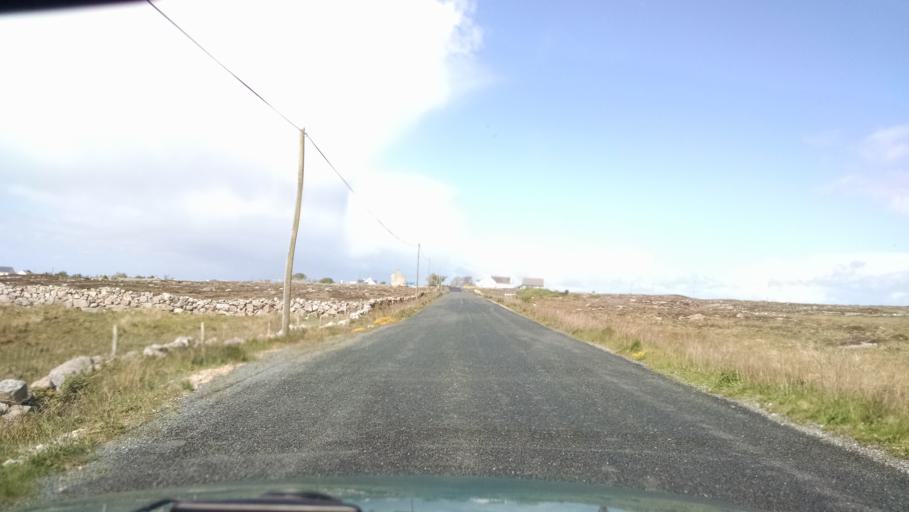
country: IE
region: Connaught
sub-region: County Galway
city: Oughterard
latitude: 53.2428
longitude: -9.5139
